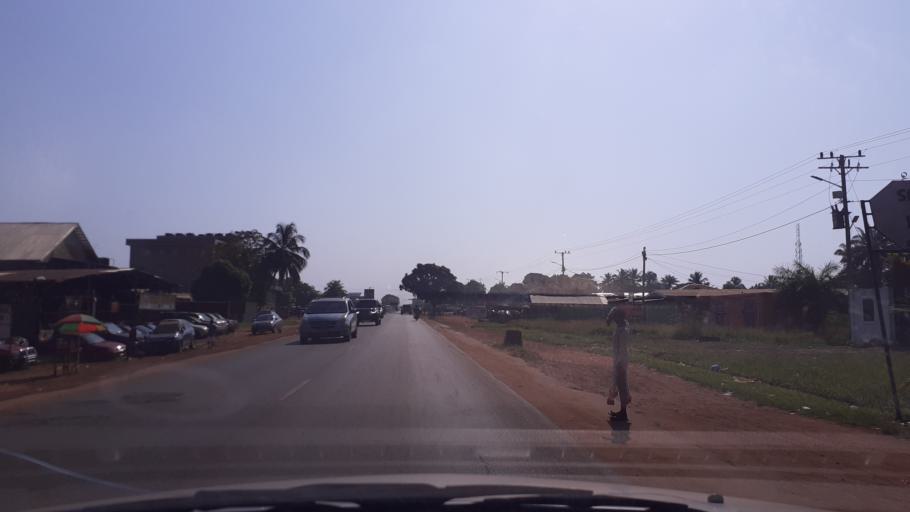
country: LR
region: Montserrado
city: Monrovia
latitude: 6.2391
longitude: -10.6869
